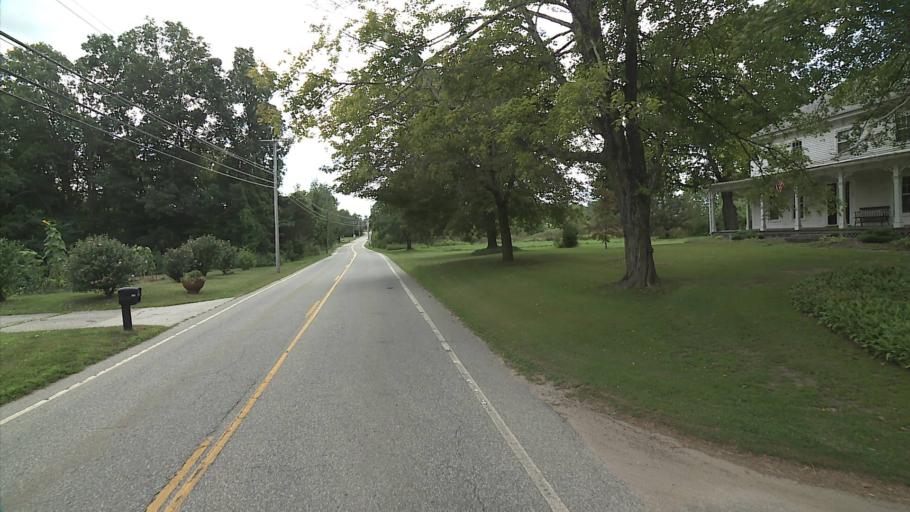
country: US
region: Connecticut
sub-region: Windham County
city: South Windham
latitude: 41.6388
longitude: -72.2095
